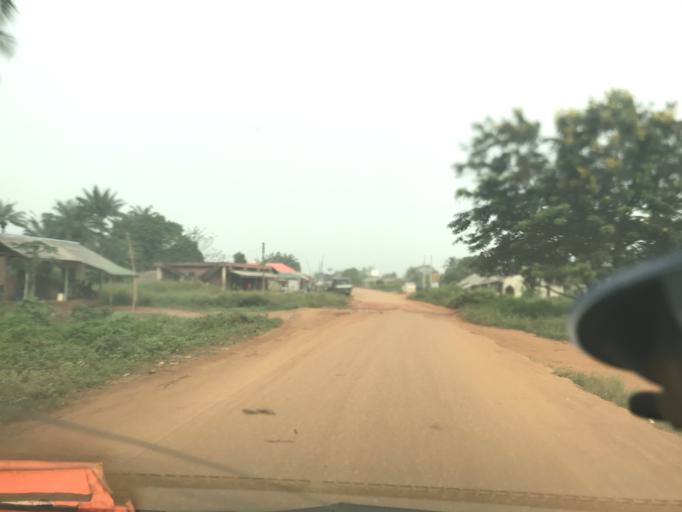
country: NG
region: Ogun
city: Ado Odo
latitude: 6.5706
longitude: 2.9409
